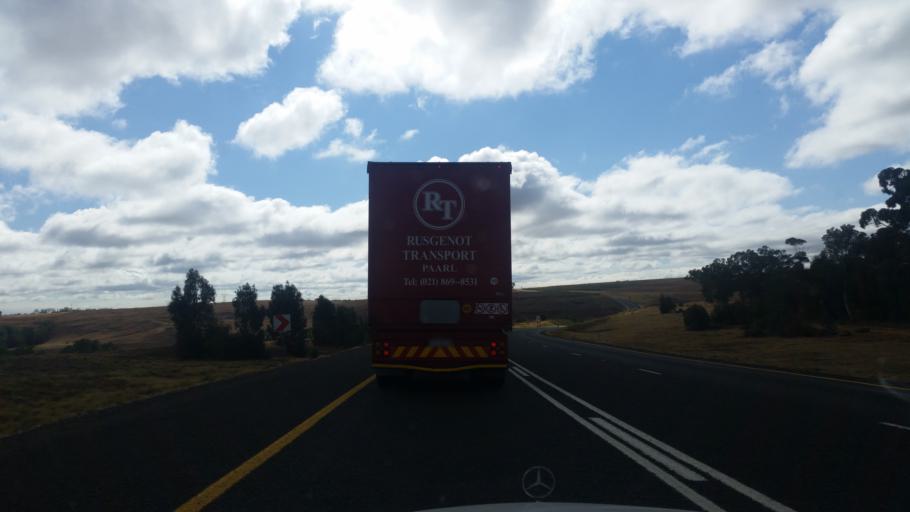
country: ZA
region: Orange Free State
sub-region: Thabo Mofutsanyana District Municipality
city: Phuthaditjhaba
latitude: -28.2719
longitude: 28.8528
